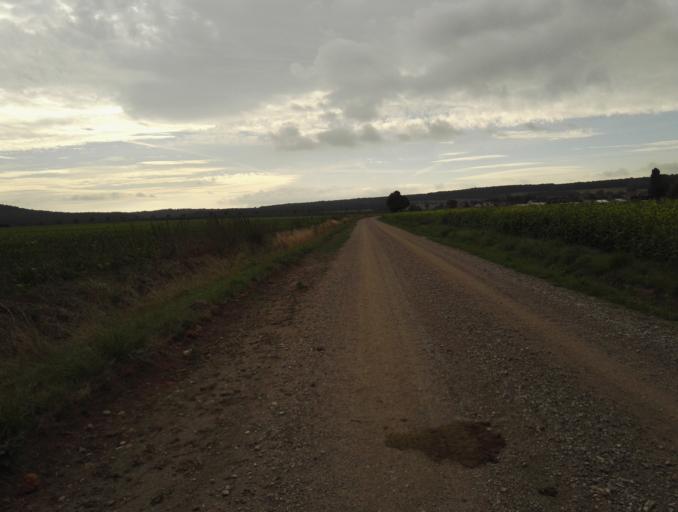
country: DE
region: Lower Saxony
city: Schellerten
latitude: 52.1453
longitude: 10.0613
